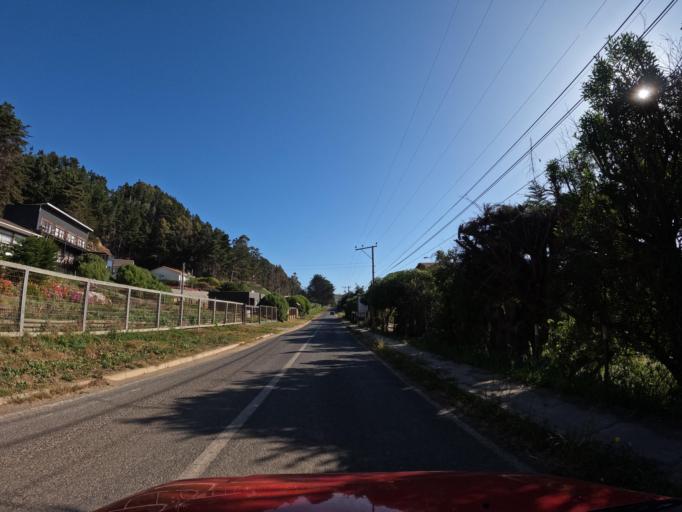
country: CL
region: Maule
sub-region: Provincia de Talca
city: Constitucion
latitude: -34.8739
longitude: -72.1522
